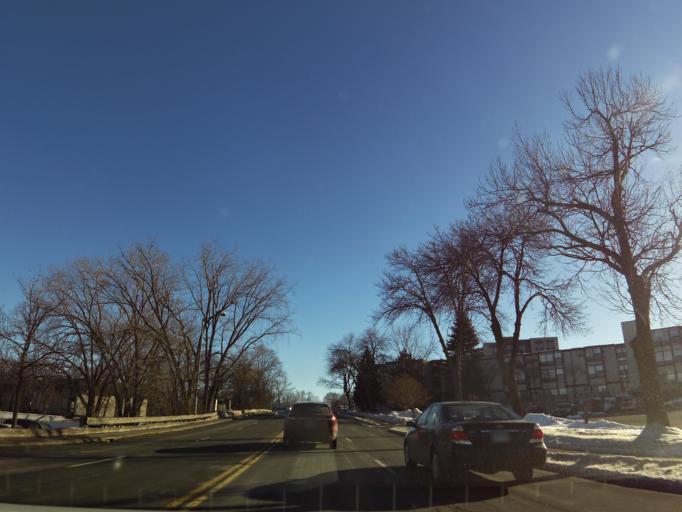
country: US
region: Minnesota
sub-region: Hennepin County
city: Saint Louis Park
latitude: 44.9361
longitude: -93.3387
